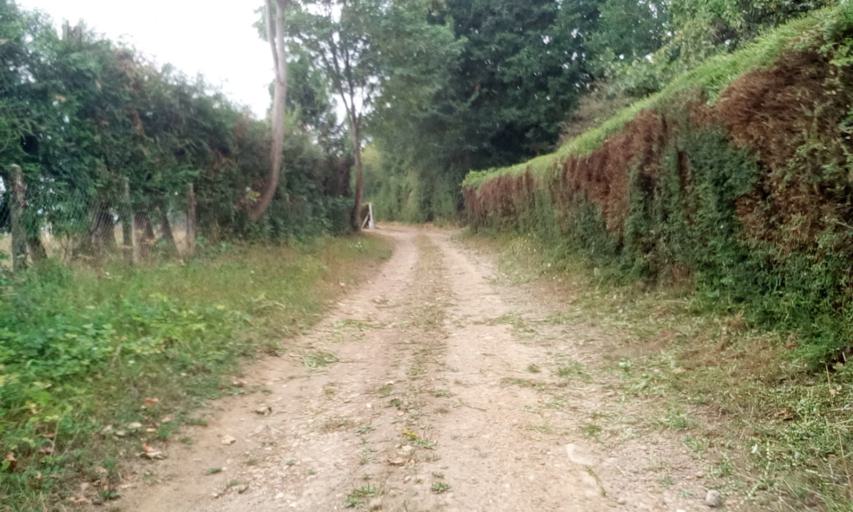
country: FR
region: Lower Normandy
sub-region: Departement du Calvados
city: Eterville
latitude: 49.1562
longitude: -0.4353
